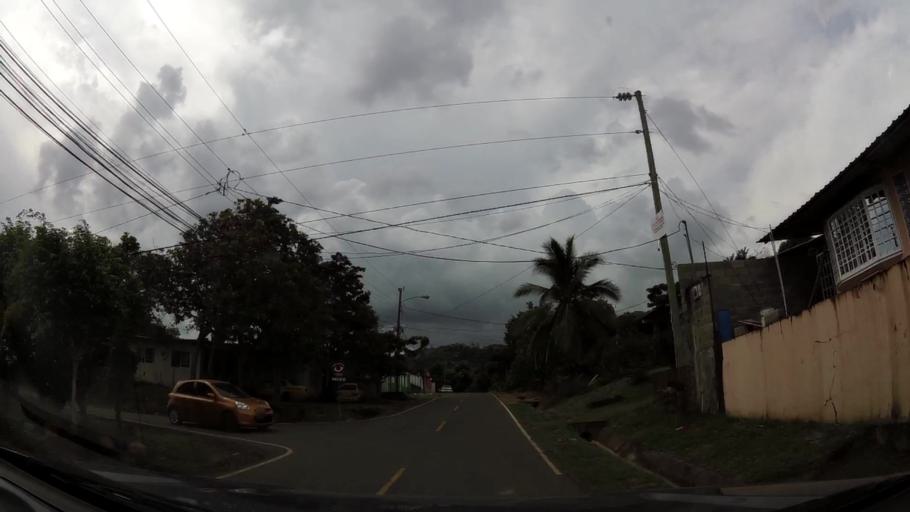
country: PA
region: Panama
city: Tocumen
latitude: 9.1125
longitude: -79.3797
